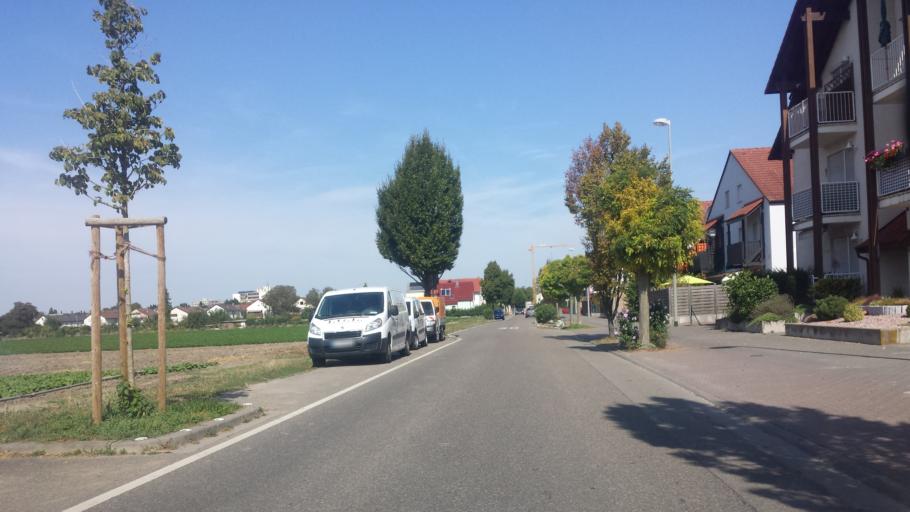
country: DE
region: Rheinland-Pfalz
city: Mutterstadt
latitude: 49.4331
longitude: 8.3568
